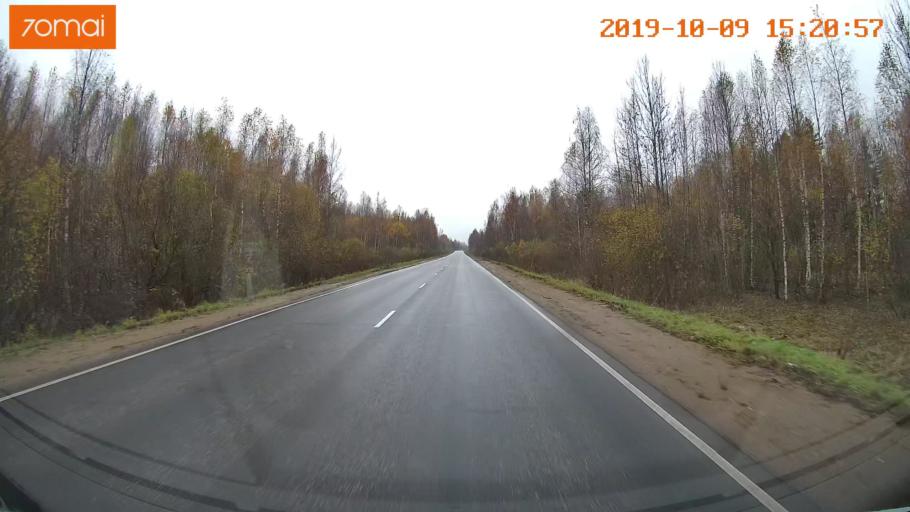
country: RU
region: Kostroma
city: Susanino
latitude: 58.0587
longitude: 41.5285
